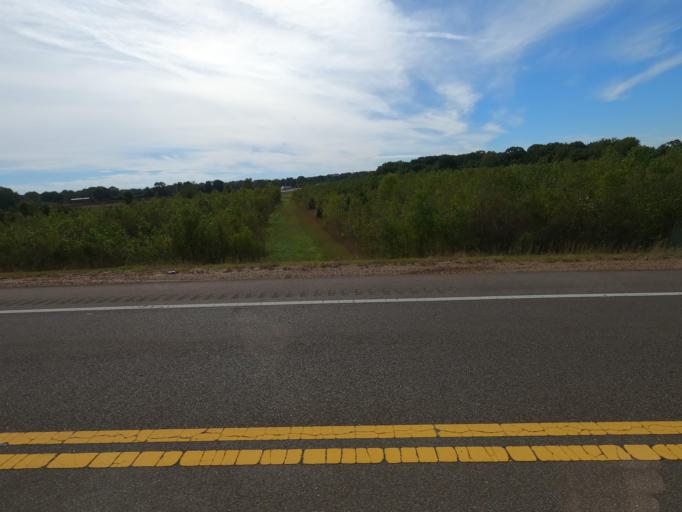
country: US
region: Tennessee
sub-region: Shelby County
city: Arlington
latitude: 35.2926
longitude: -89.6119
